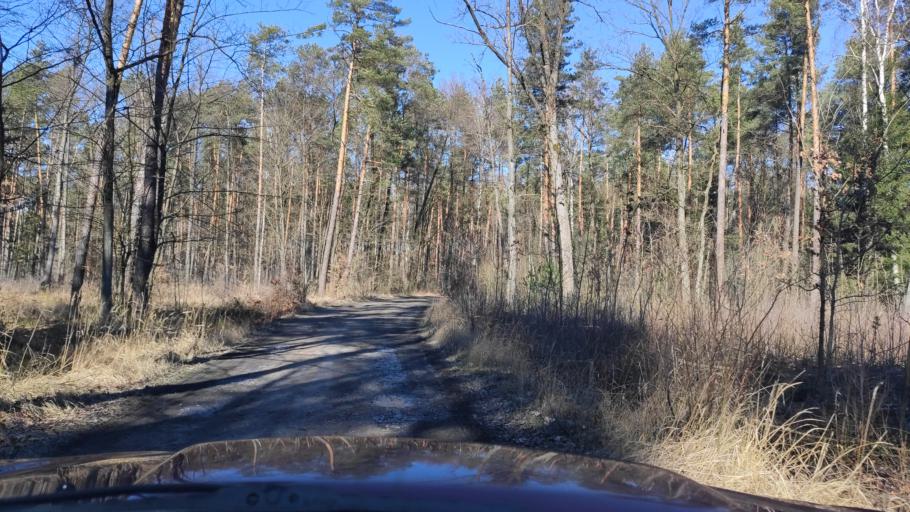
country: PL
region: Masovian Voivodeship
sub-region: Powiat kozienicki
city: Garbatka-Letnisko
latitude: 51.4450
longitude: 21.5354
